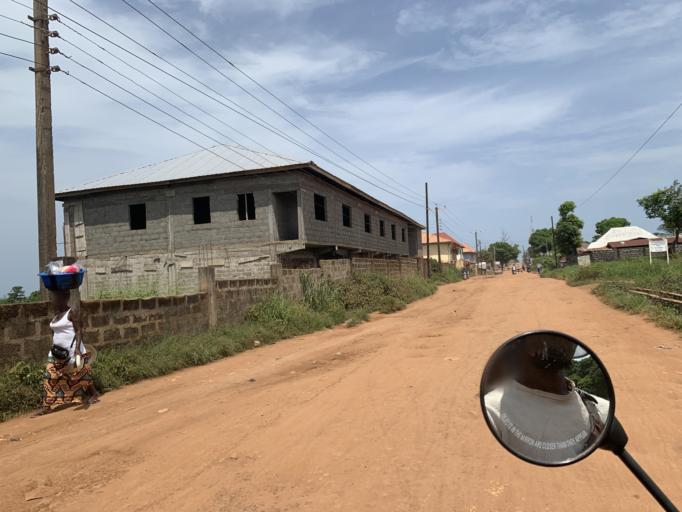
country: SL
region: Western Area
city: Hastings
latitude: 8.4042
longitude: -13.1359
